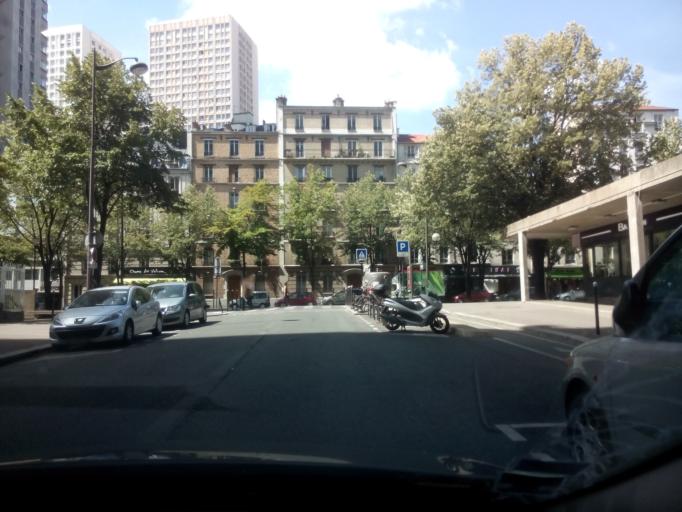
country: FR
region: Ile-de-France
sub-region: Departement du Val-de-Marne
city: Le Kremlin-Bicetre
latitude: 48.8304
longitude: 2.3582
